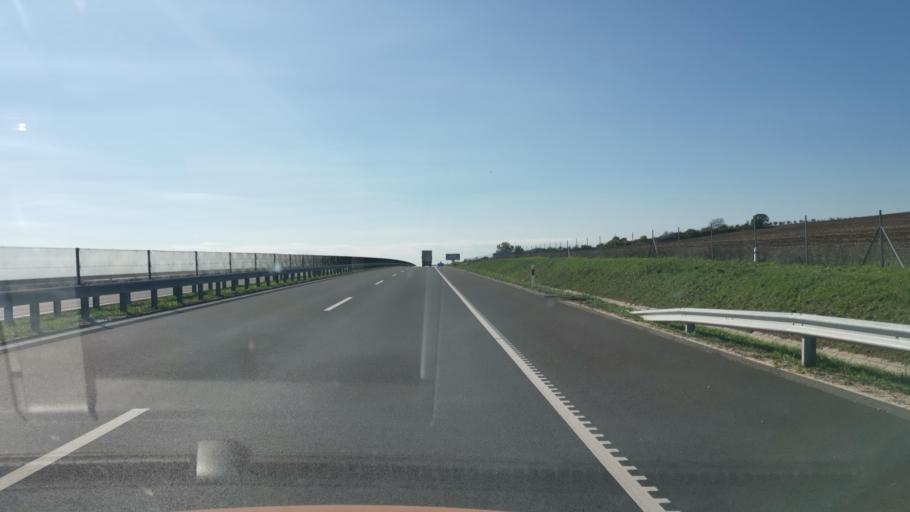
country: HU
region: Borsod-Abauj-Zemplen
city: Halmaj
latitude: 48.2637
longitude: 20.9908
